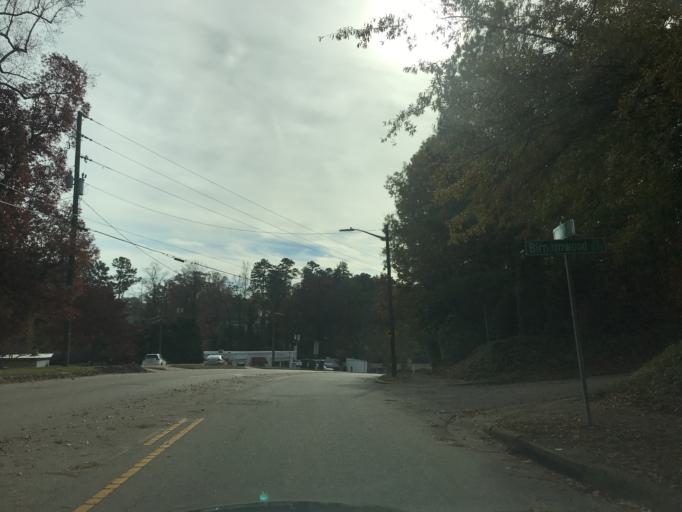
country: US
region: North Carolina
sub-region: Wake County
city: West Raleigh
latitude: 35.8110
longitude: -78.6768
